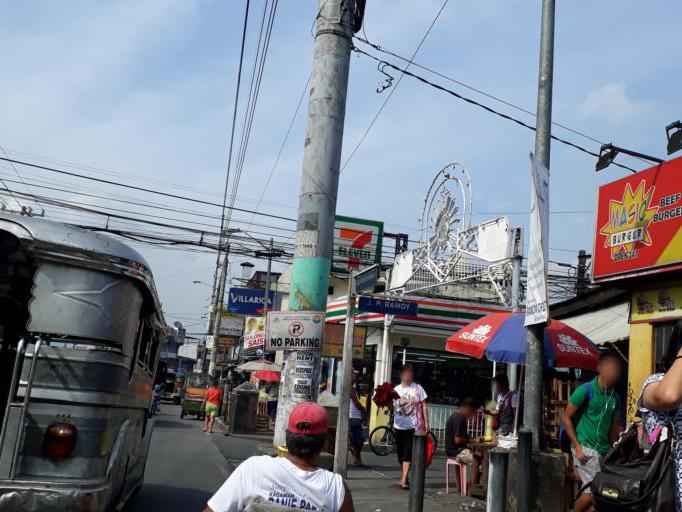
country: PH
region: Calabarzon
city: Bagong Pagasa
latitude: 14.6862
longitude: 121.0242
